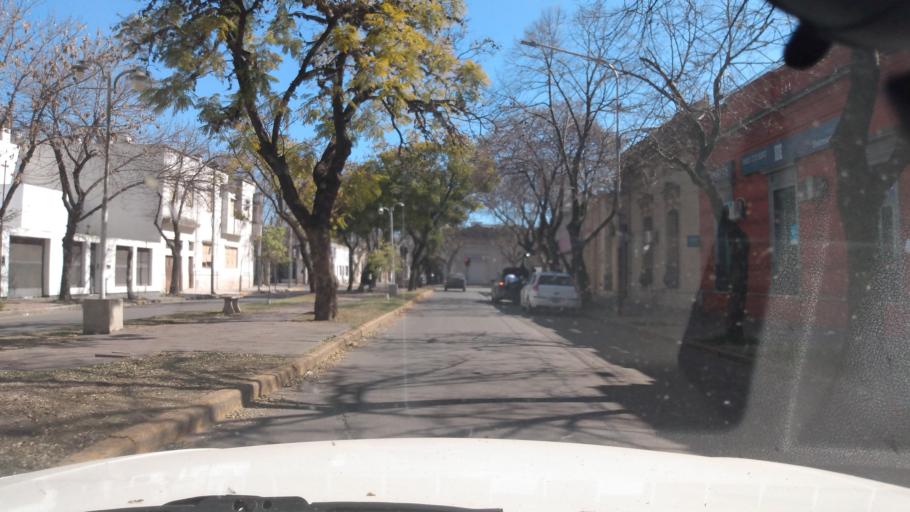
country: AR
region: Buenos Aires
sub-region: Partido de Mercedes
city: Mercedes
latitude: -34.6488
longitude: -59.4306
